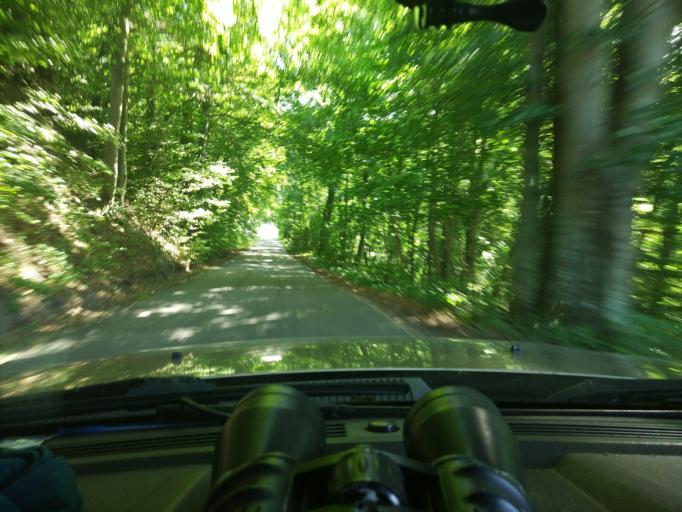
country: PL
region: Pomeranian Voivodeship
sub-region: Powiat wejherowski
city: Choczewo
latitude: 54.7603
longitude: 17.7918
